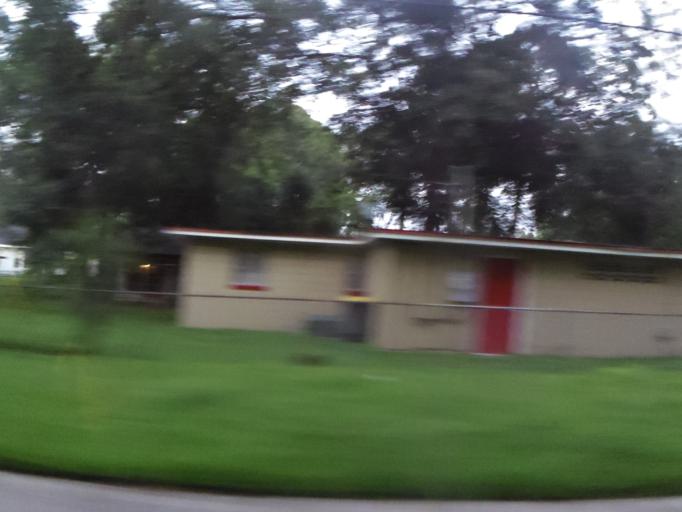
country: US
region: Florida
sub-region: Duval County
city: Jacksonville
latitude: 30.3199
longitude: -81.7137
